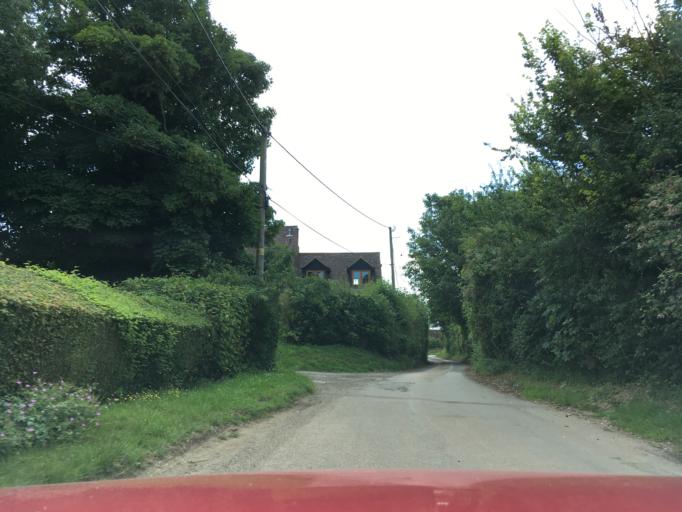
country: GB
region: England
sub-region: Buckinghamshire
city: Winslow
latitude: 51.9375
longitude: -0.8288
